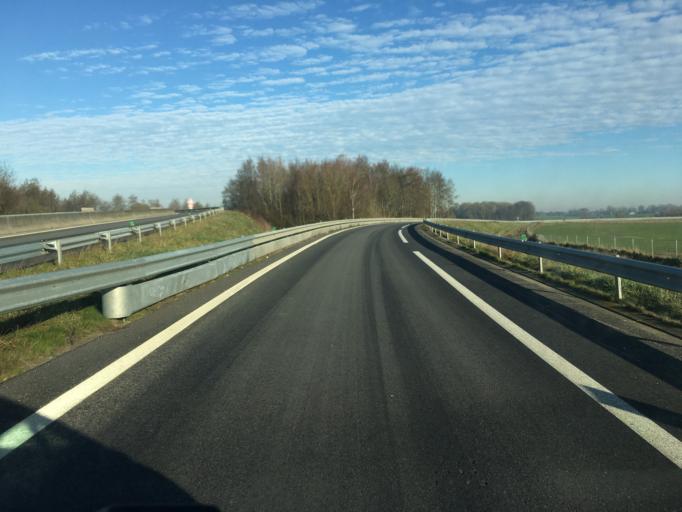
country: FR
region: Haute-Normandie
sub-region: Departement de la Seine-Maritime
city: Yerville
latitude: 49.6504
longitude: 0.8449
